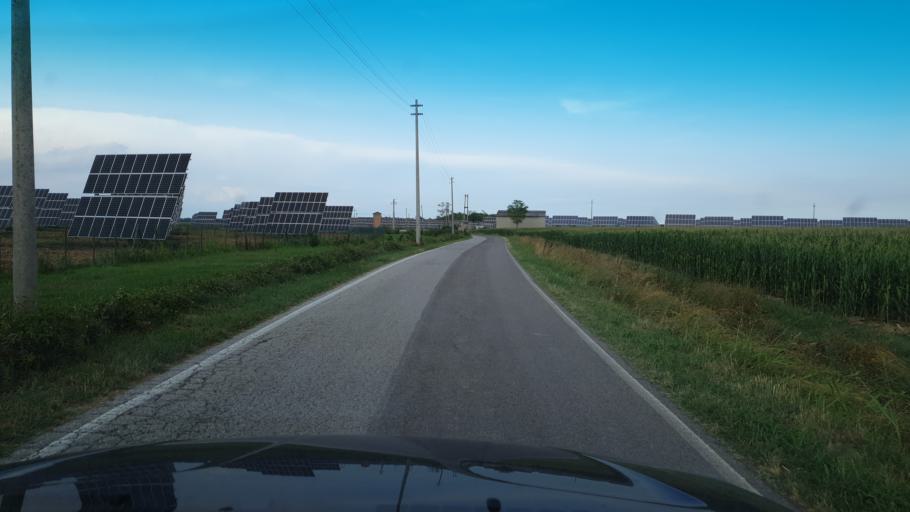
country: IT
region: Veneto
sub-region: Provincia di Rovigo
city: Castelguglielmo
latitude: 45.0025
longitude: 11.5348
